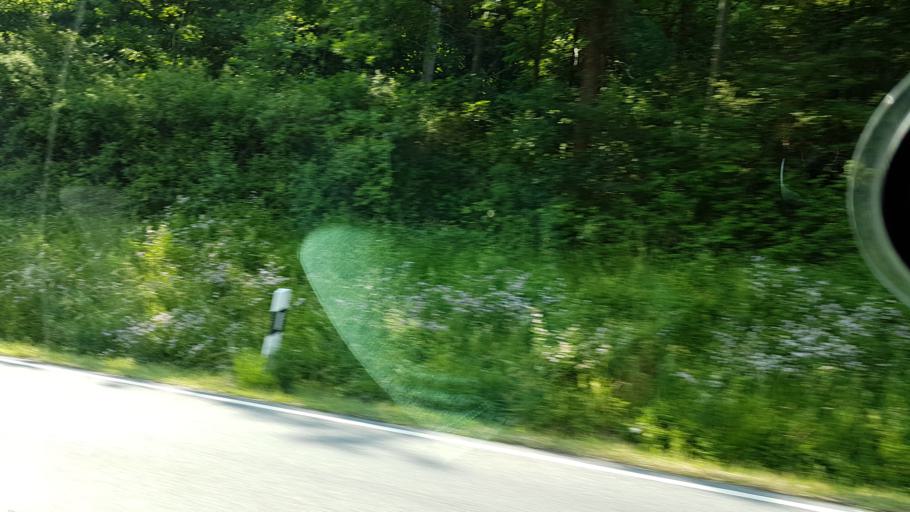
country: DE
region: Rheinland-Pfalz
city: Odenbach
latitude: 49.6806
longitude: 7.6326
